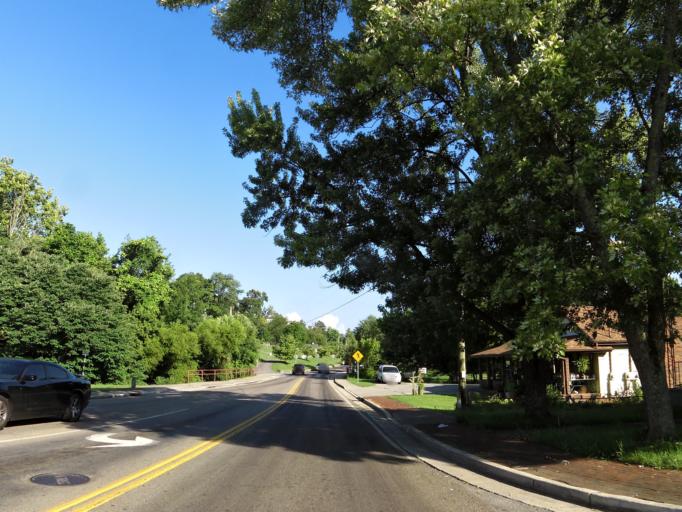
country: US
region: Tennessee
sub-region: Blount County
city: Maryville
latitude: 35.7505
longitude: -83.9732
